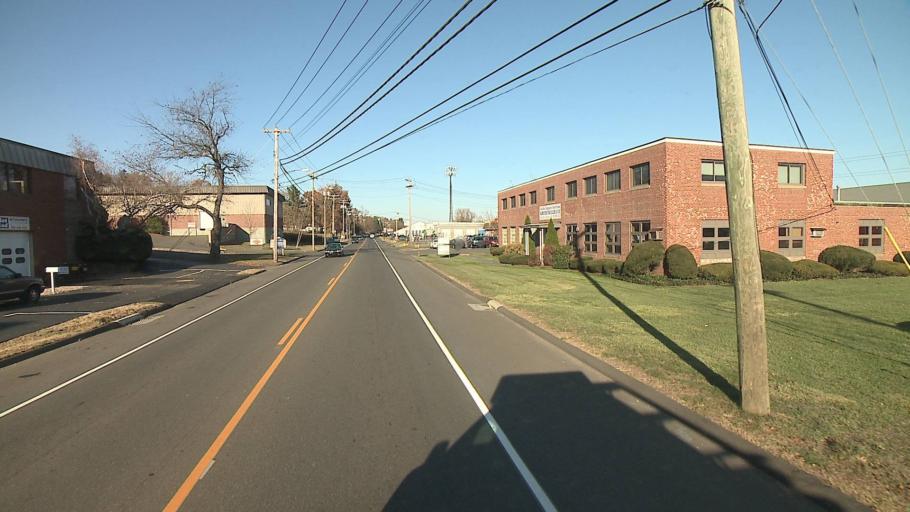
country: US
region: Connecticut
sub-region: New Haven County
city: Hamden
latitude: 41.3535
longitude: -72.8915
